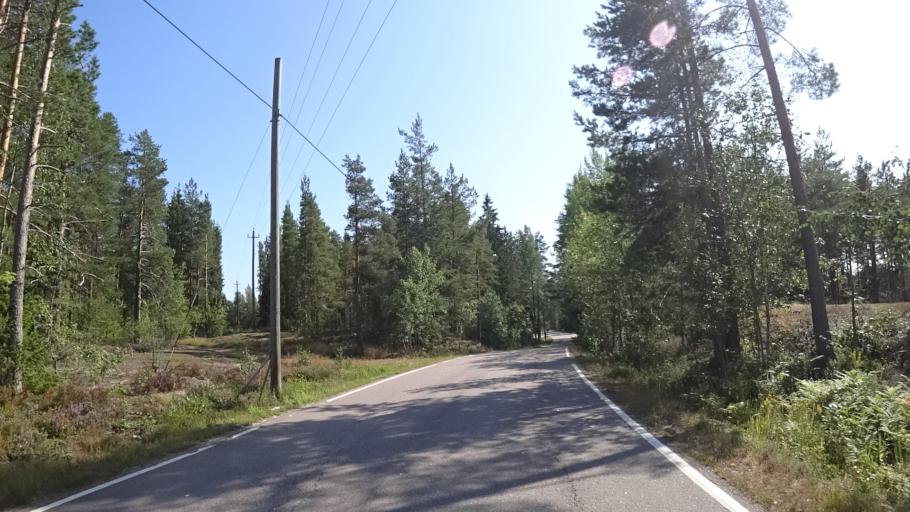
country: FI
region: Kymenlaakso
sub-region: Kotka-Hamina
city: Karhula
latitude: 60.5592
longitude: 26.9002
